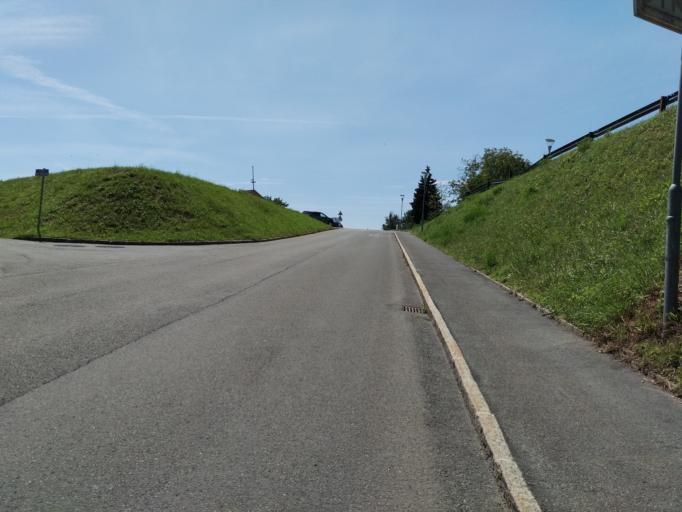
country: AT
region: Styria
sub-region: Politischer Bezirk Graz-Umgebung
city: Feldkirchen bei Graz
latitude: 46.9933
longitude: 15.4524
